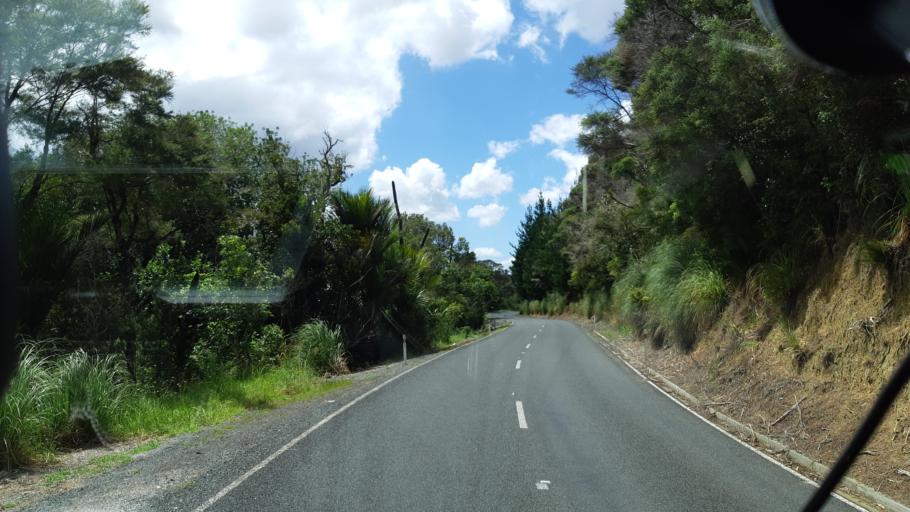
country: NZ
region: Northland
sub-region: Far North District
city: Taipa
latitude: -35.2533
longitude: 173.5331
